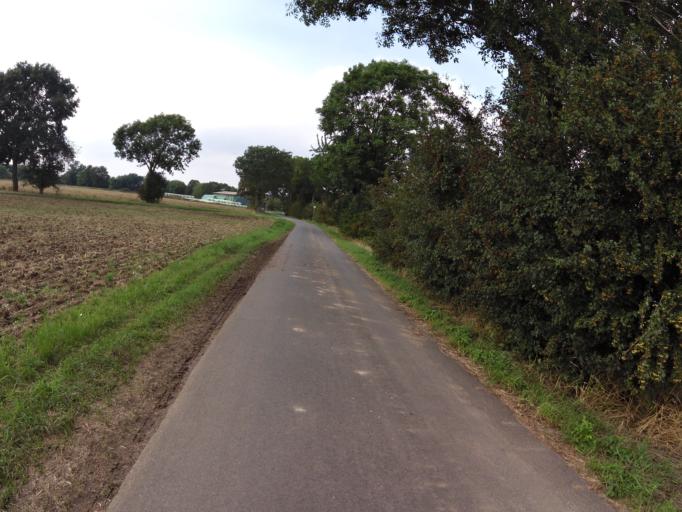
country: DE
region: Lower Saxony
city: Hilgermissen
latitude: 52.8860
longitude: 9.1724
